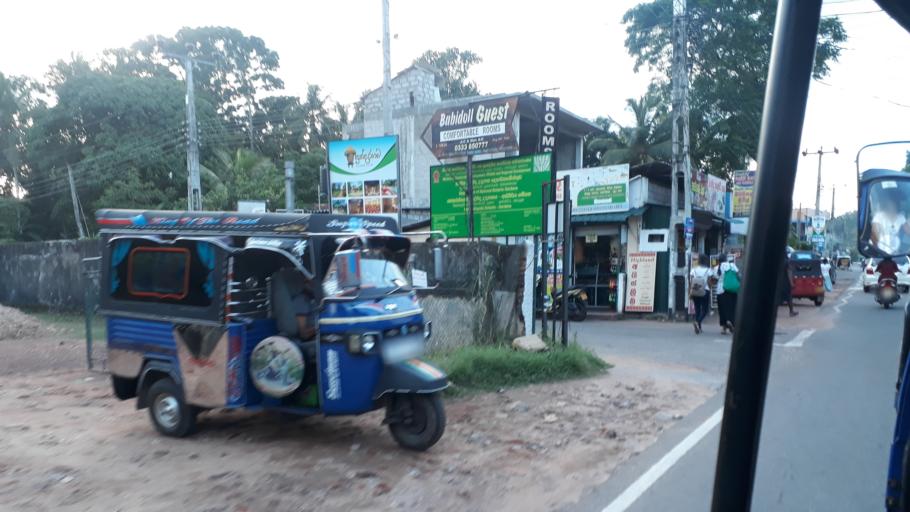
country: LK
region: Western
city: Gampaha
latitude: 7.1019
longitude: 79.9908
